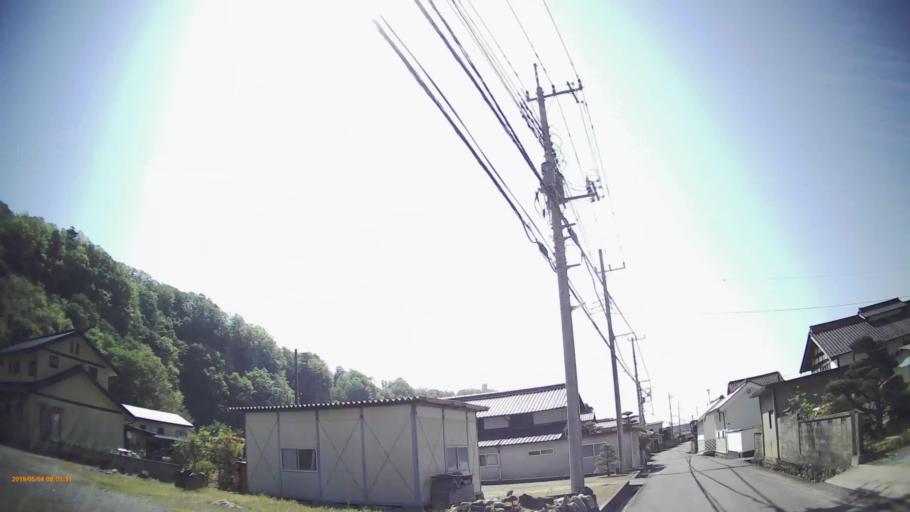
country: JP
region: Yamanashi
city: Nirasaki
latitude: 35.7289
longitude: 138.4259
